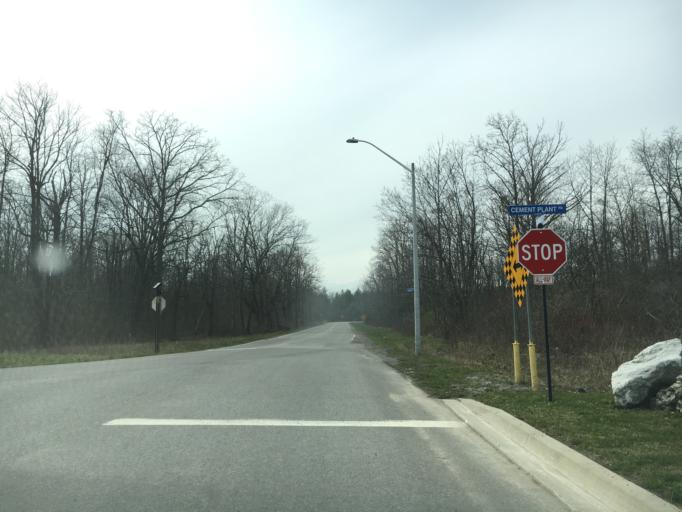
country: CA
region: Ontario
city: Port Colborne
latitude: 42.8838
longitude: -79.2803
